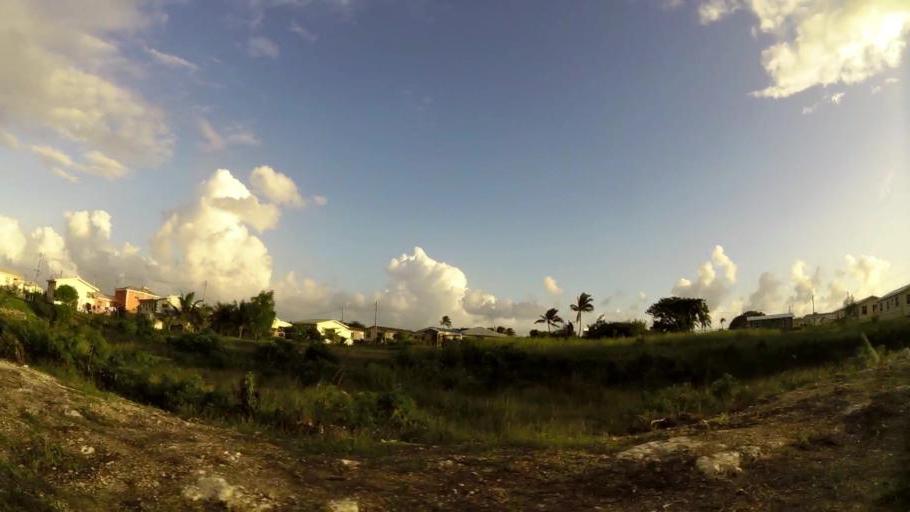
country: BB
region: Saint Philip
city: Crane
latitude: 13.1150
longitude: -59.4739
